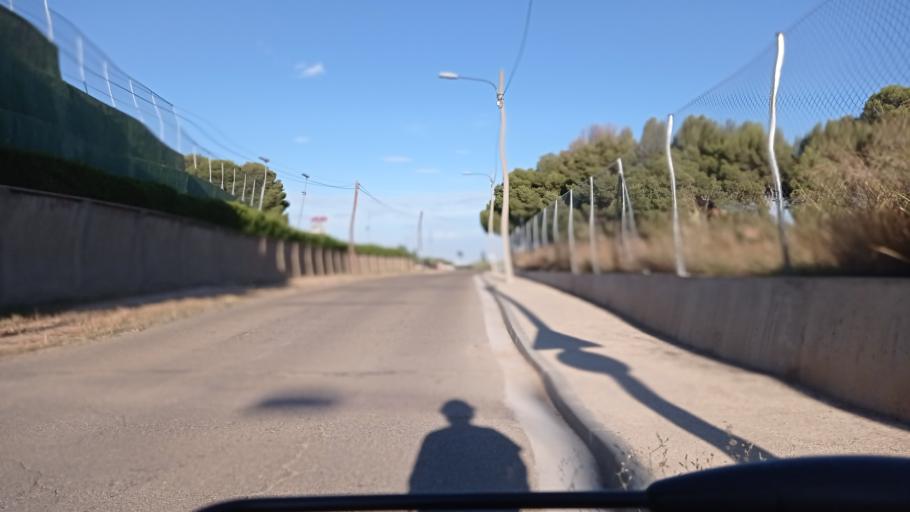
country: ES
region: Aragon
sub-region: Provincia de Zaragoza
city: Oliver-Valdefierro, Oliver, Valdefierro
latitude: 41.6746
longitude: -0.9578
